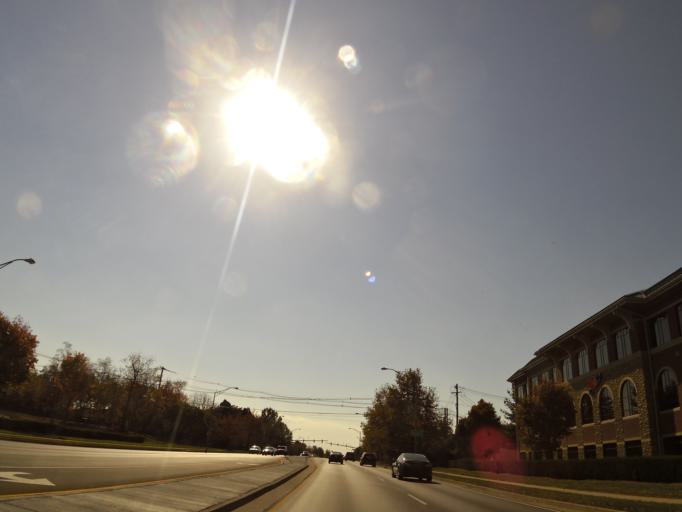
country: US
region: Kentucky
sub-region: Fayette County
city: Lexington-Fayette
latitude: 38.0143
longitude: -84.4204
